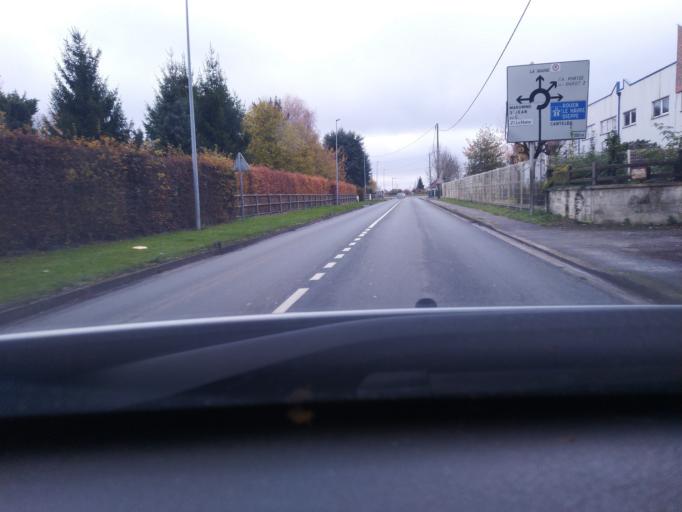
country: FR
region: Haute-Normandie
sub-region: Departement de la Seine-Maritime
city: Maromme
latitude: 49.4850
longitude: 1.0124
